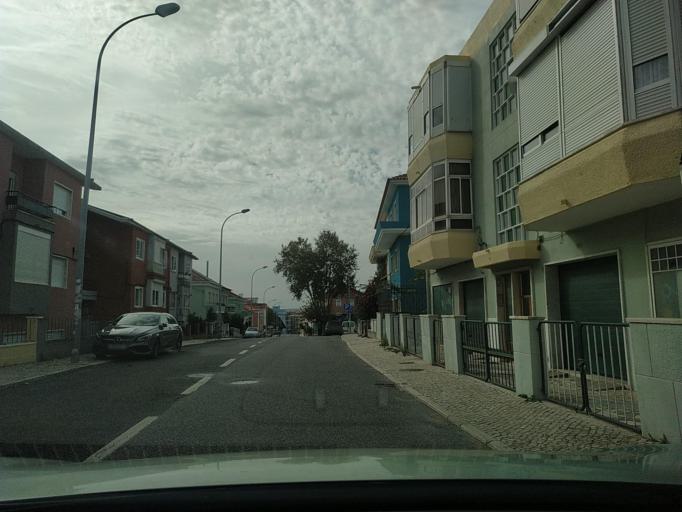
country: PT
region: Lisbon
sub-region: Amadora
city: Amadora
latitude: 38.7639
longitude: -9.2326
